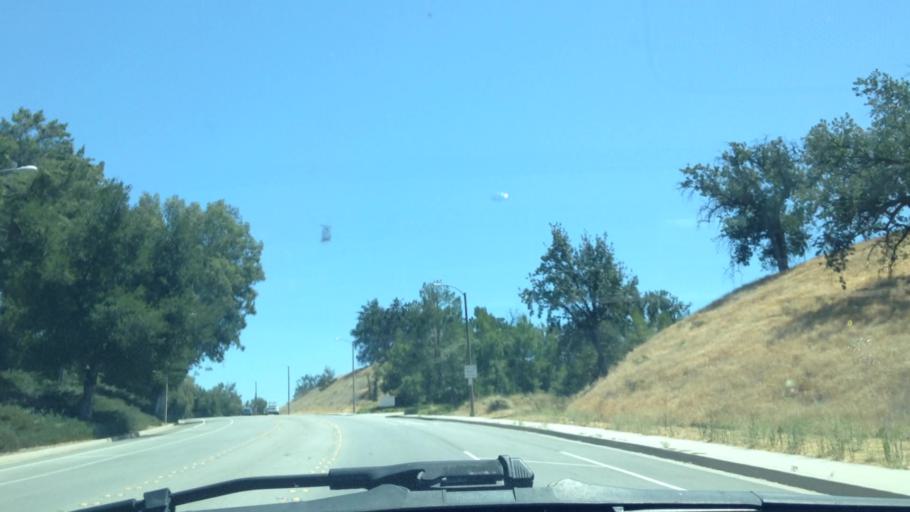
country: US
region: California
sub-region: Los Angeles County
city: Santa Clarita
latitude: 34.3987
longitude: -118.5667
